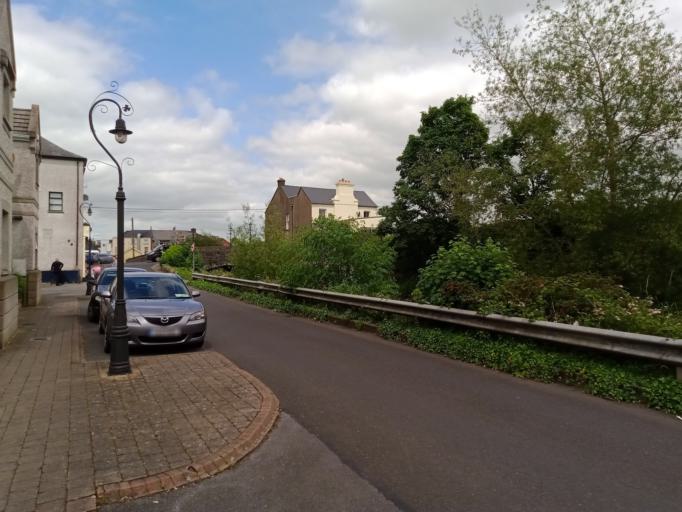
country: IE
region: Leinster
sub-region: County Carlow
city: Carlow
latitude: 52.8362
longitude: -6.9385
